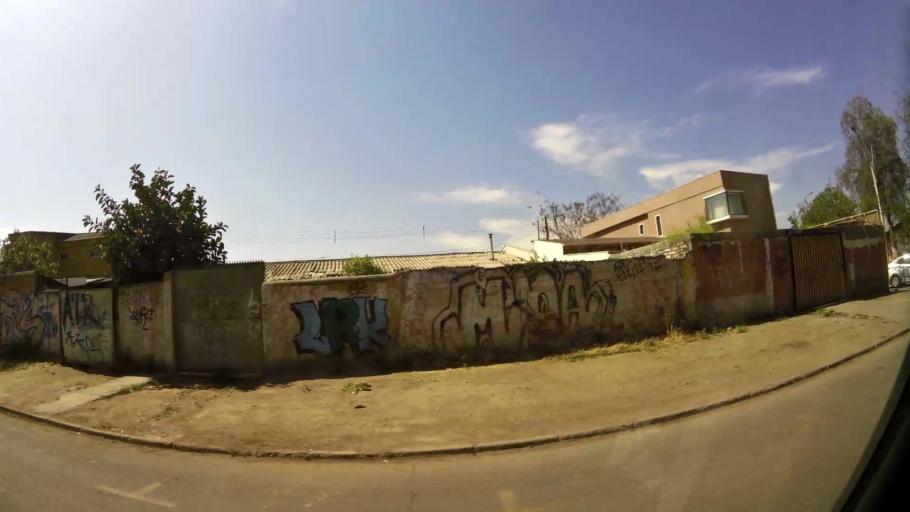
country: CL
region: Santiago Metropolitan
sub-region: Provincia de Santiago
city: Lo Prado
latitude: -33.4640
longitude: -70.7009
